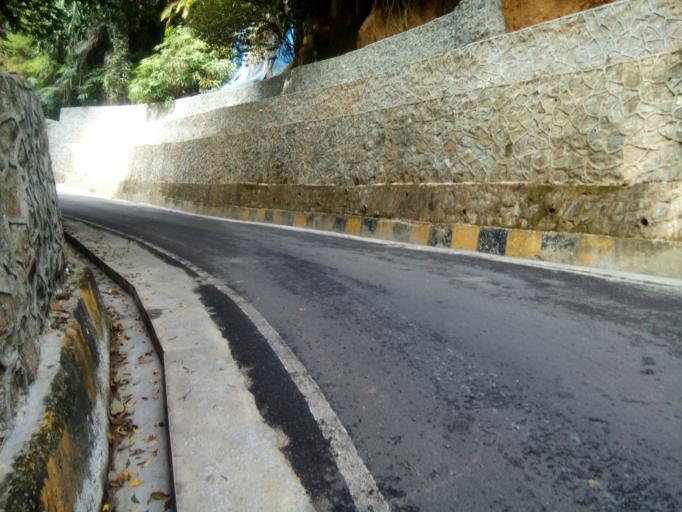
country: MY
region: Penang
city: Tanjung Tokong
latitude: 5.4371
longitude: 100.2860
